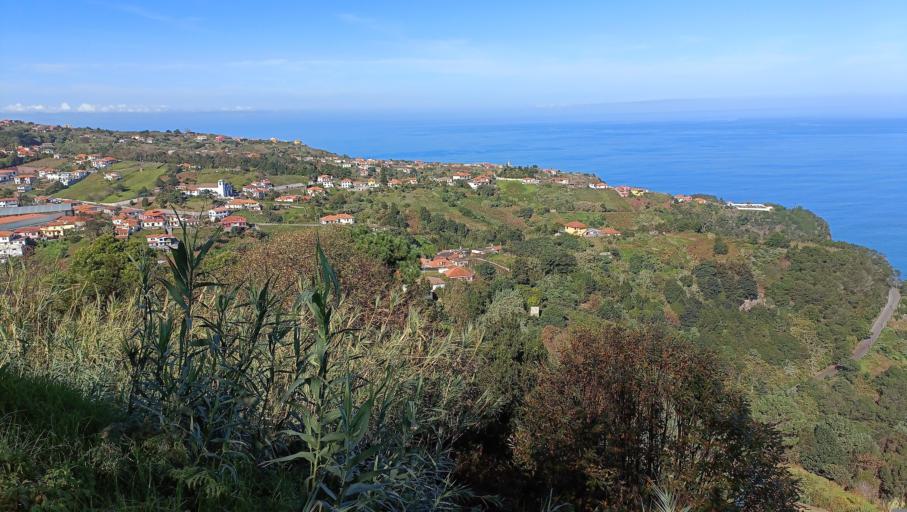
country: PT
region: Madeira
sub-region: Santana
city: Santana
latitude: 32.8226
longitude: -16.9023
